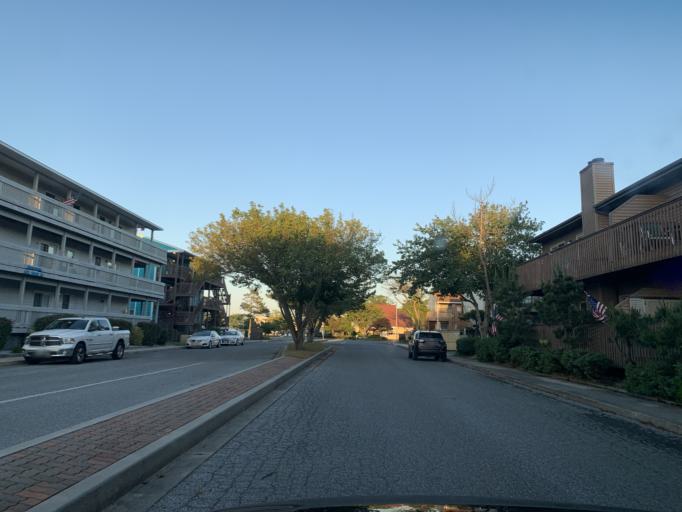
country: US
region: Delaware
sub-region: Sussex County
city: Bethany Beach
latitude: 38.4498
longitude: -75.0568
